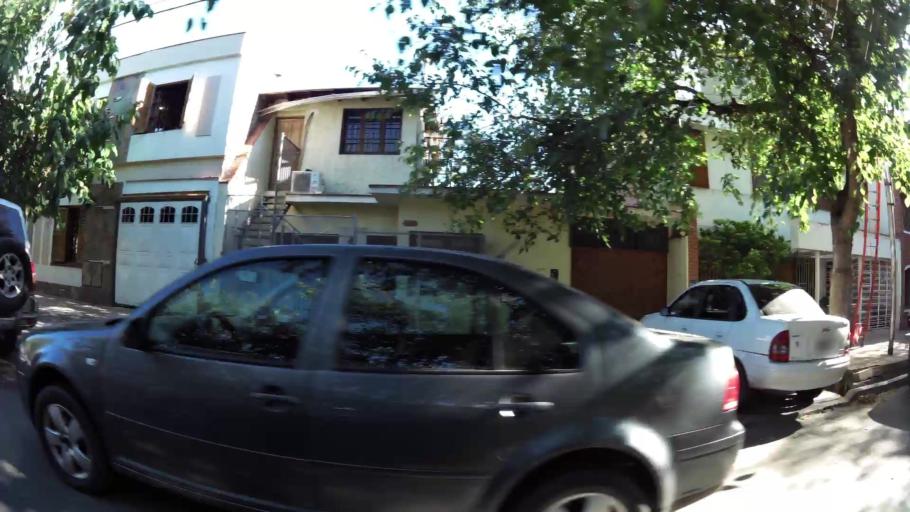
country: AR
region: Mendoza
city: Las Heras
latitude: -32.8662
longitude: -68.8380
